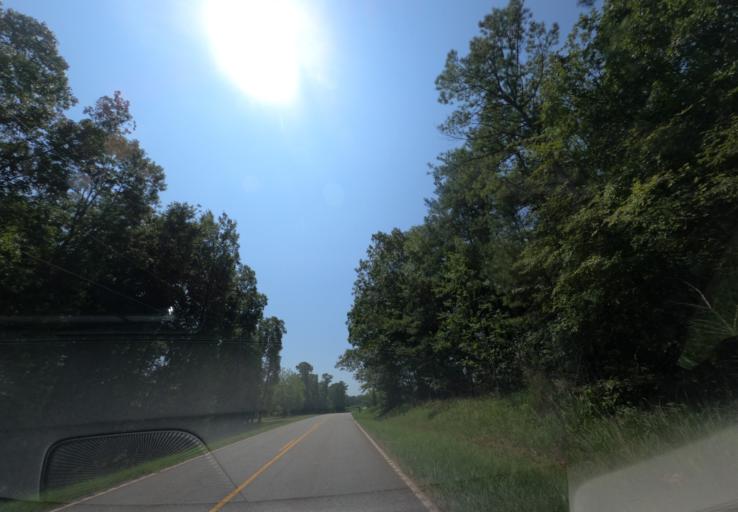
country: US
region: South Carolina
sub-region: Greenwood County
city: Greenwood
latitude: 34.0603
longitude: -82.1408
